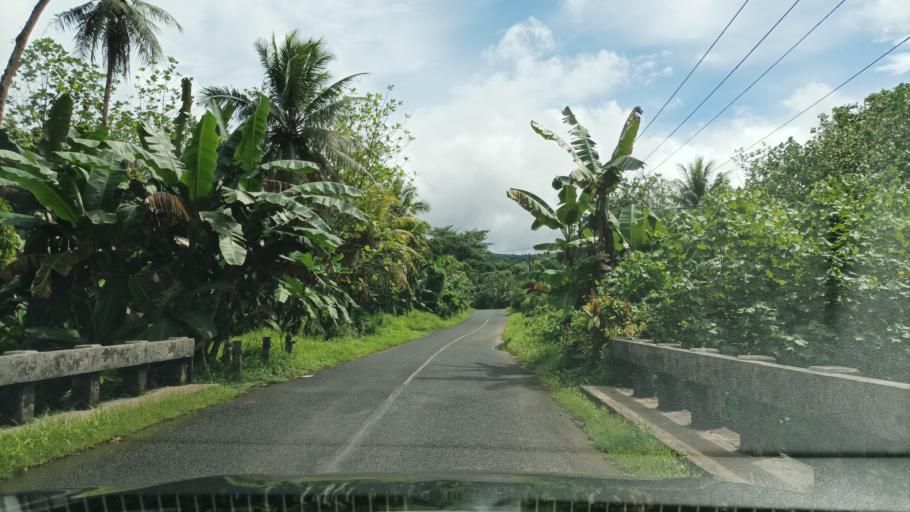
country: FM
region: Pohnpei
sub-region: Madolenihm Municipality
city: Madolenihm Municipality Government
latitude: 6.8869
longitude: 158.2910
